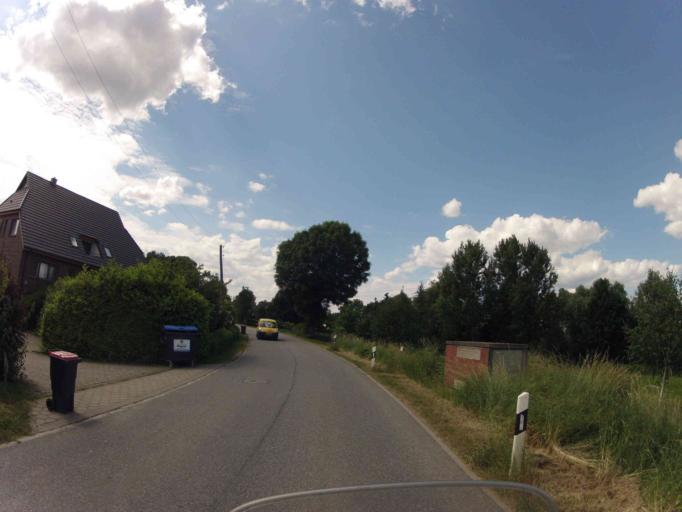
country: DE
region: Lower Saxony
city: Stelle
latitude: 53.4637
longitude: 10.1233
